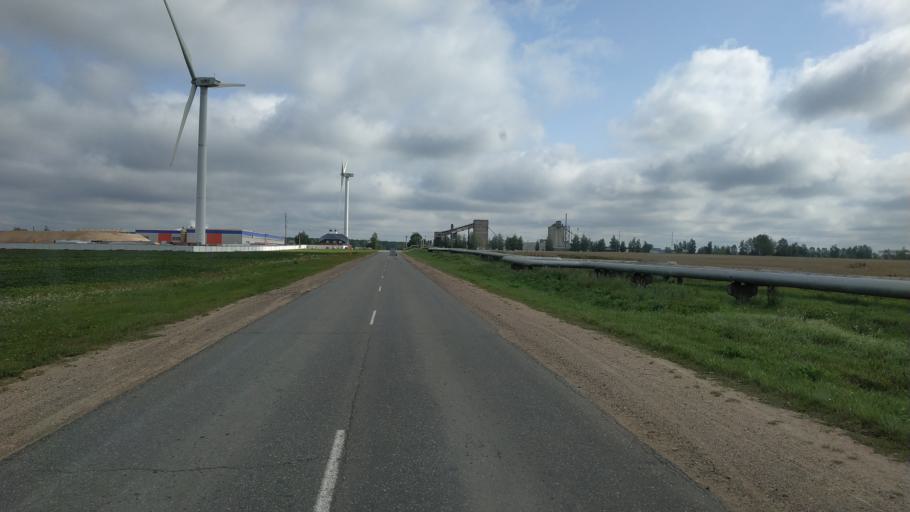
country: BY
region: Mogilev
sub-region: Mahilyowski Rayon
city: Veyno
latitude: 53.8379
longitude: 30.3728
